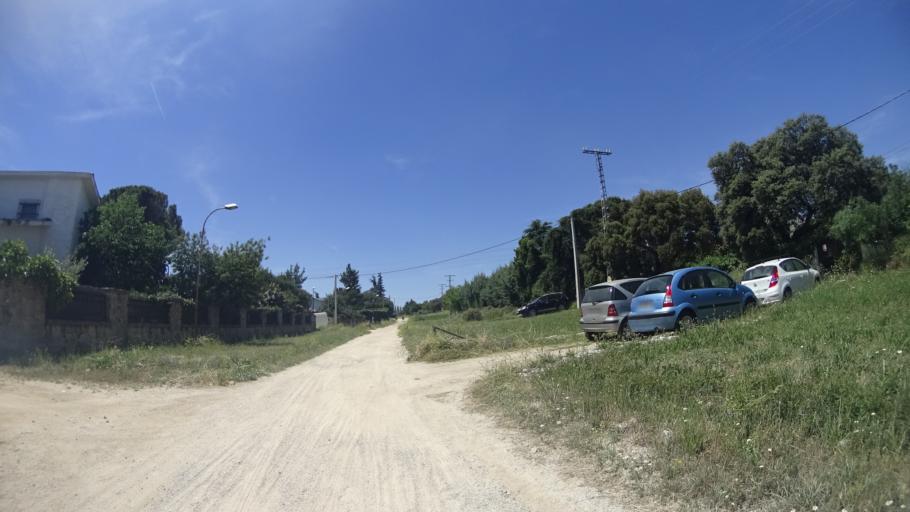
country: ES
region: Madrid
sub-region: Provincia de Madrid
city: Navalquejigo
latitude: 40.6211
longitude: -4.0319
